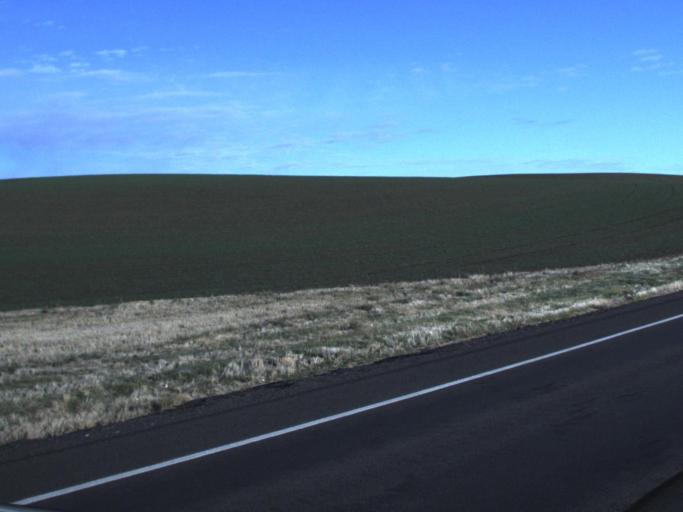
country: US
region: Washington
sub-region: Garfield County
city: Pomeroy
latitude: 46.7726
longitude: -117.7054
